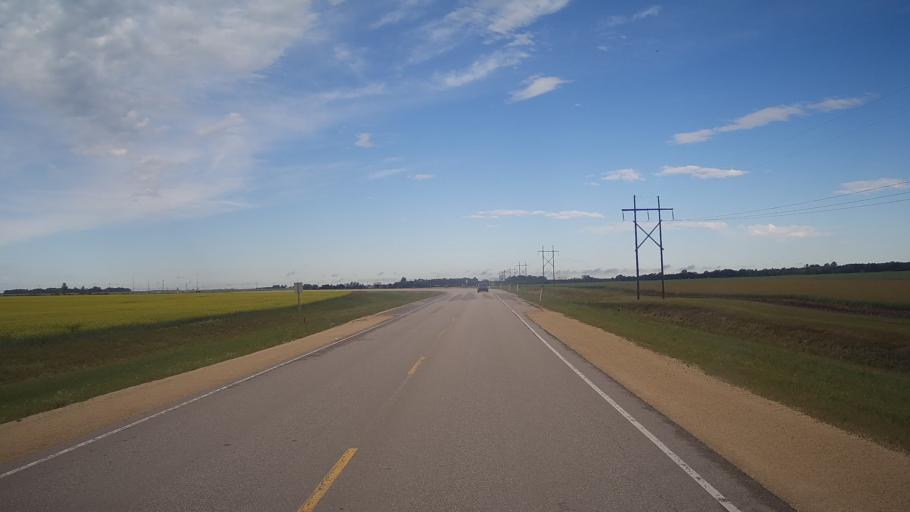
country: CA
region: Manitoba
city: Stonewall
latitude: 50.1227
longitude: -97.5190
